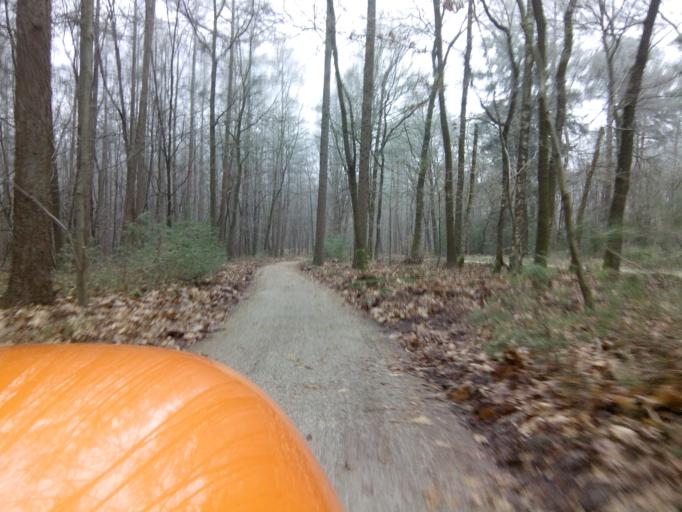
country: NL
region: Gelderland
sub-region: Gemeente Putten
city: Putten
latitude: 52.2574
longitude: 5.6373
